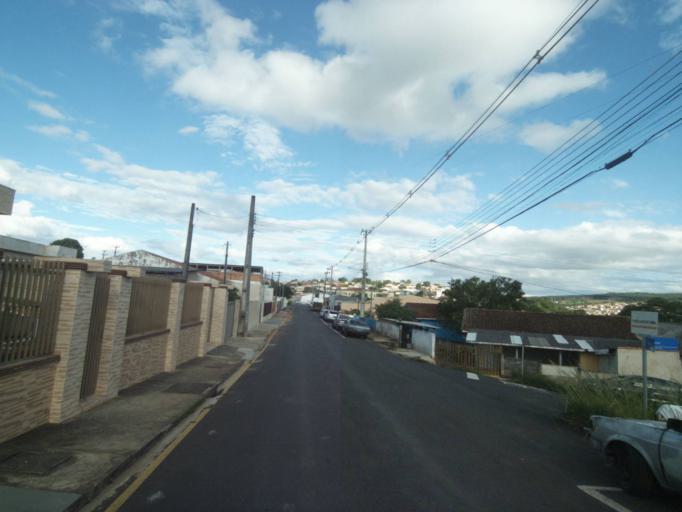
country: BR
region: Parana
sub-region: Telemaco Borba
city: Telemaco Borba
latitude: -24.3371
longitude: -50.6181
